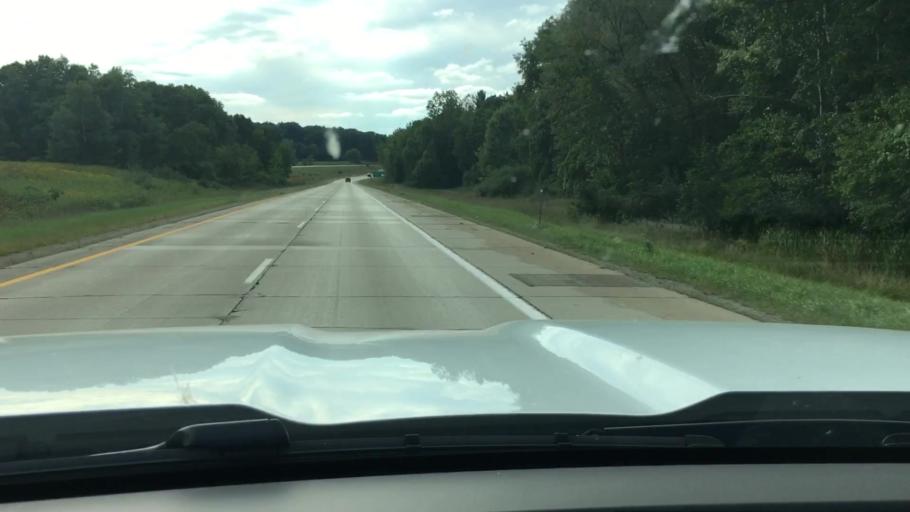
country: US
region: Michigan
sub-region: Lapeer County
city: Lapeer
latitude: 43.0083
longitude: -83.2083
